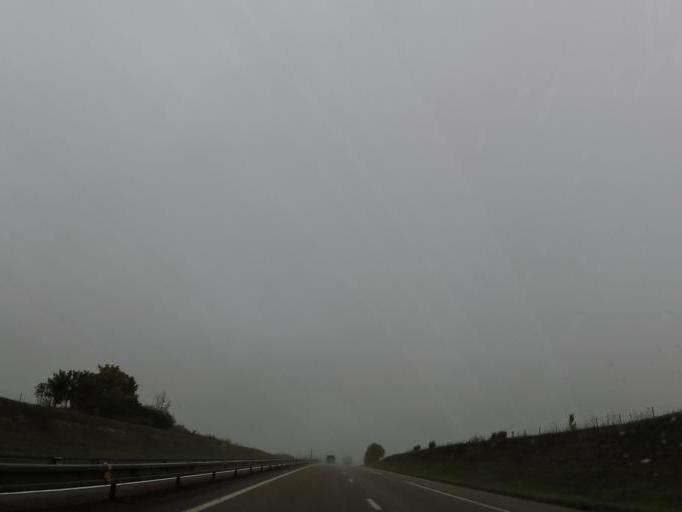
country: FR
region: Champagne-Ardenne
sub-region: Departement de la Marne
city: Gueux
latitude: 49.2363
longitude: 3.8686
